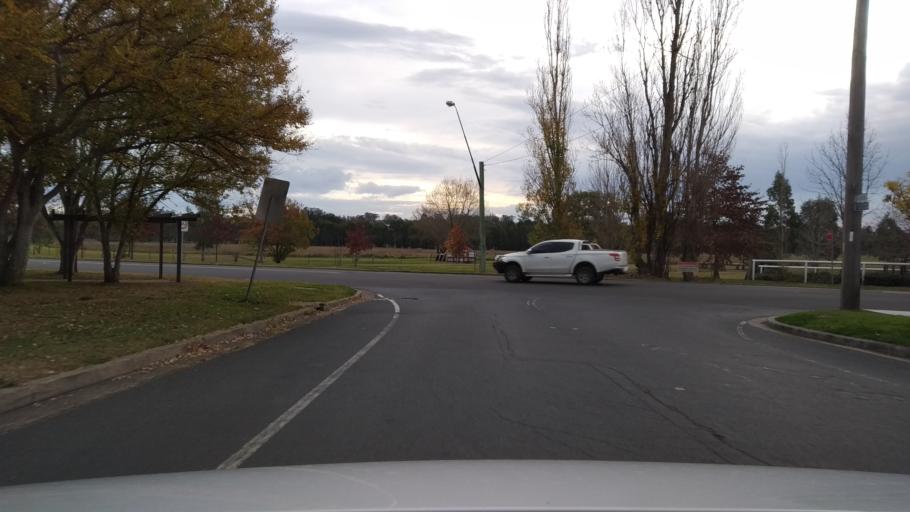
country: AU
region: New South Wales
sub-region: Camden
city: Elderslie
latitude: -34.0583
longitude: 150.6912
